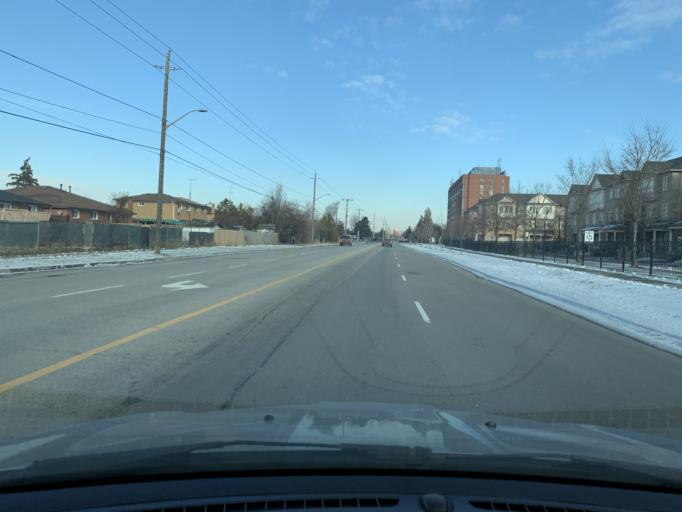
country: CA
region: Ontario
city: Etobicoke
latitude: 43.7174
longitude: -79.6274
